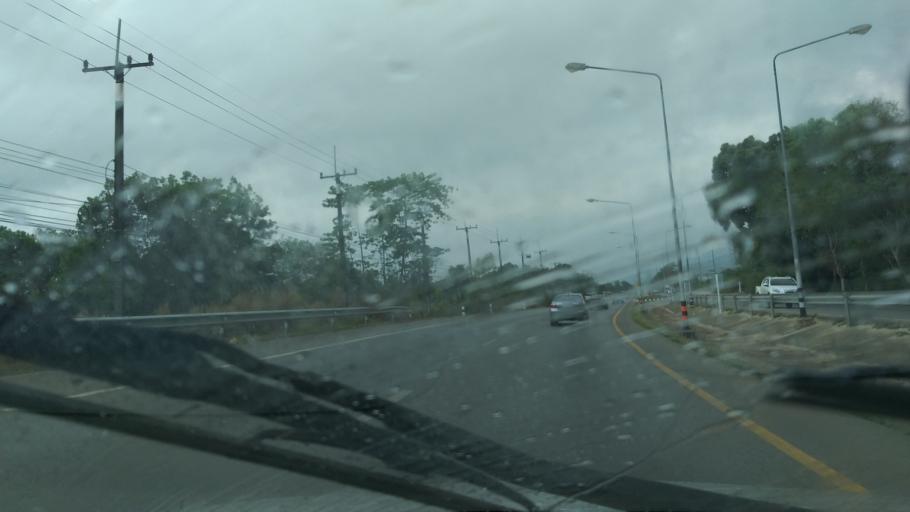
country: TH
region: Chanthaburi
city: Khlung
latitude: 12.4512
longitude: 102.2447
